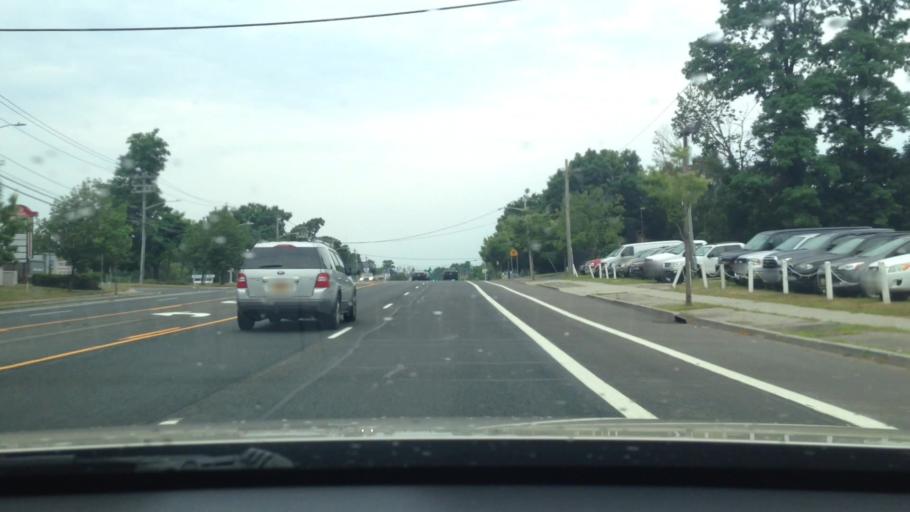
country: US
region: New York
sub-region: Suffolk County
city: Selden
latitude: 40.8672
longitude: -73.0311
